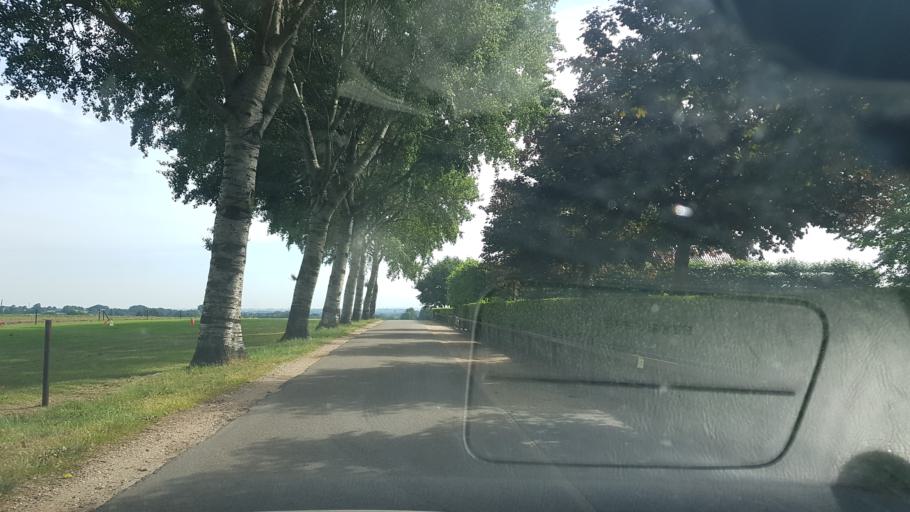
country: NL
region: Gelderland
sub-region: Gemeente Groesbeek
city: Bredeweg
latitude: 51.7615
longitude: 5.9259
